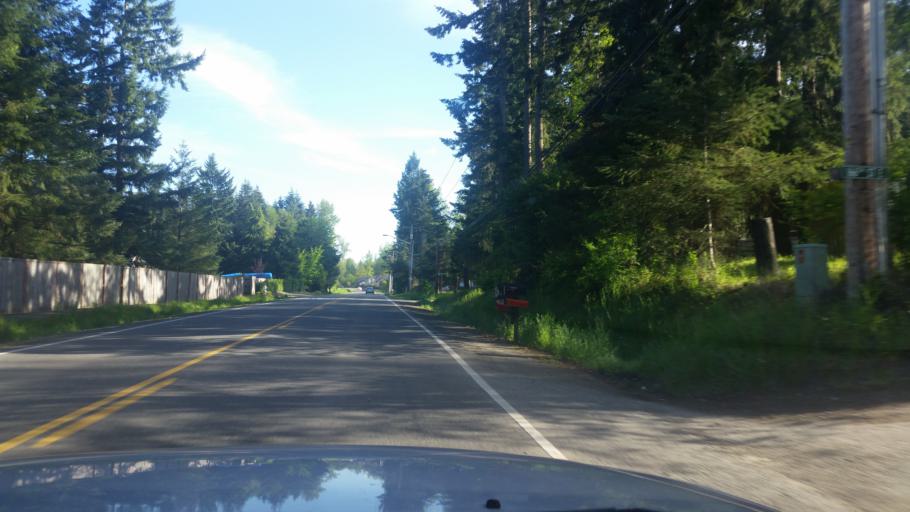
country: US
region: Washington
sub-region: Pierce County
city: South Hill
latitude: 47.1057
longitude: -122.2669
